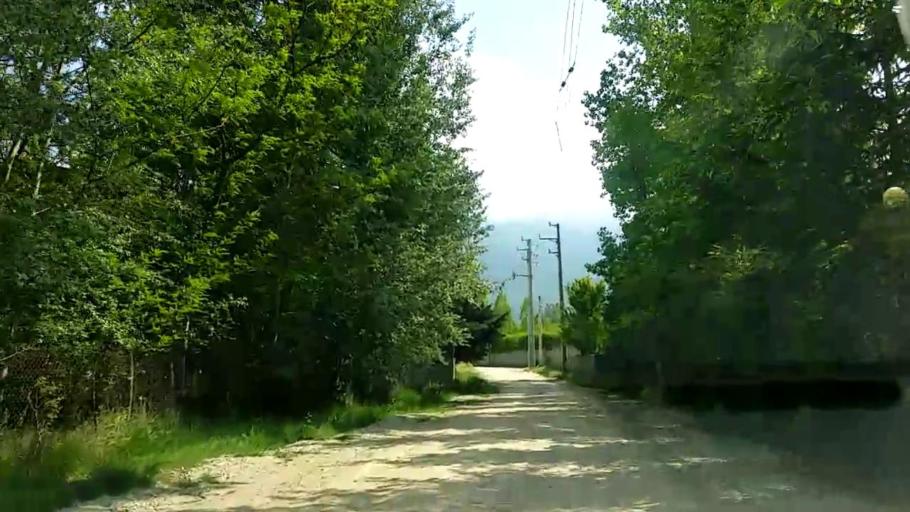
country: IR
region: Mazandaran
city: `Abbasabad
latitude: 36.5248
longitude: 51.1830
